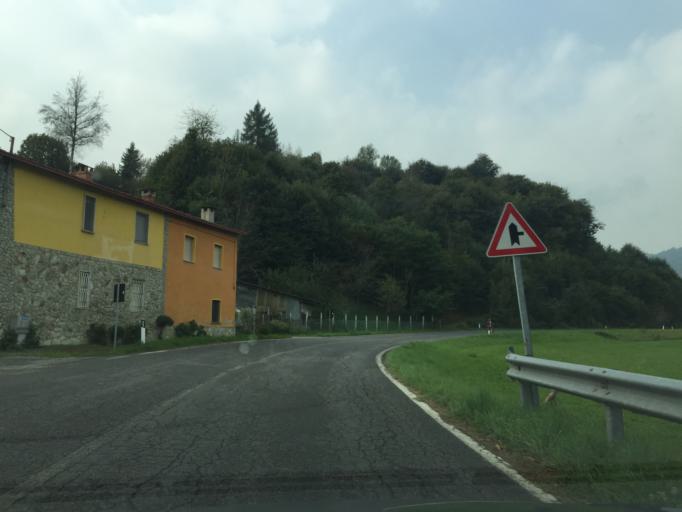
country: IT
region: Piedmont
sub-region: Provincia di Cuneo
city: Roccaforte Mondovi
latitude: 44.3113
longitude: 7.7227
